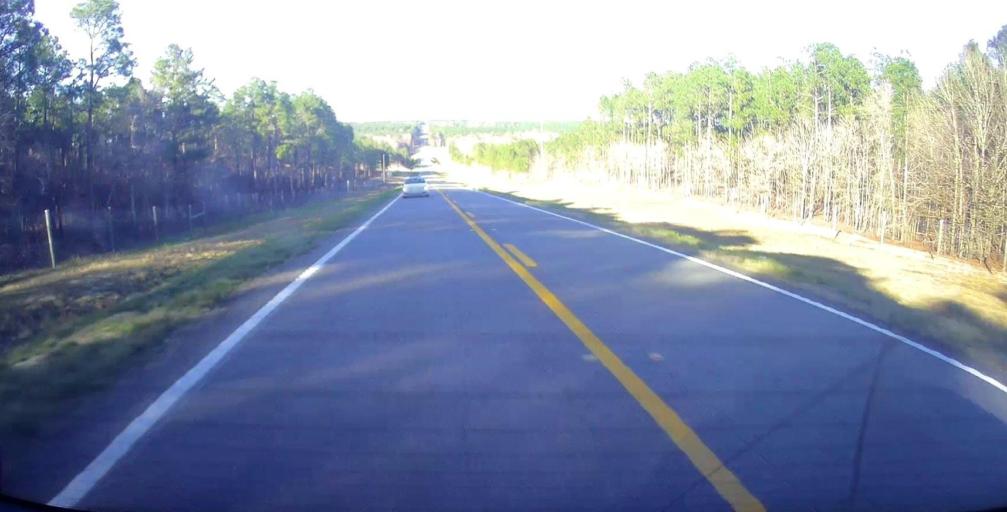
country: US
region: Georgia
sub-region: Taylor County
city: Butler
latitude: 32.4980
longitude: -84.3388
